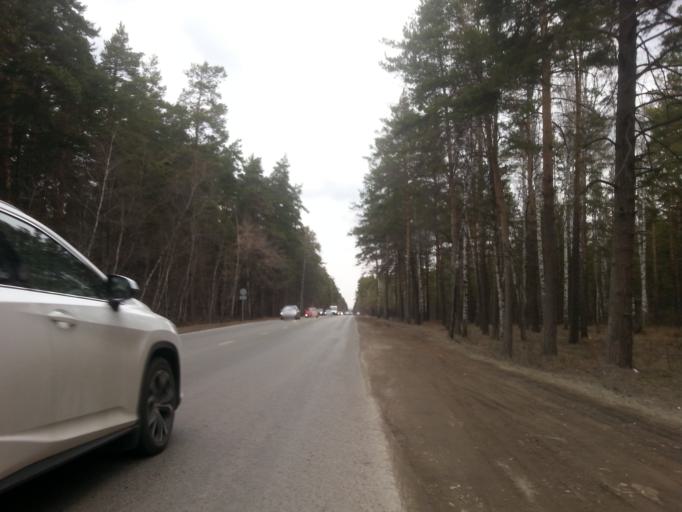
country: RU
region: Altai Krai
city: Yuzhnyy
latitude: 53.2724
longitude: 83.7233
